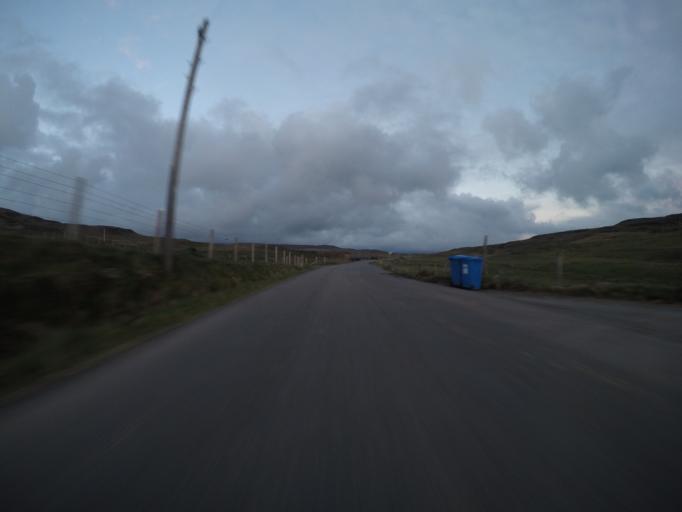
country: GB
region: Scotland
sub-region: Highland
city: Portree
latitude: 57.5998
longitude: -6.3763
